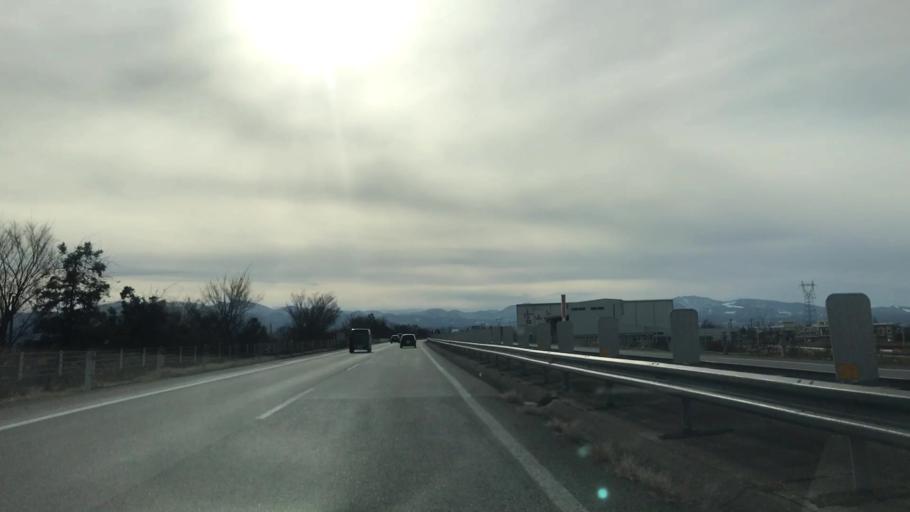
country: JP
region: Toyama
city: Toyama-shi
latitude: 36.6564
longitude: 137.2575
